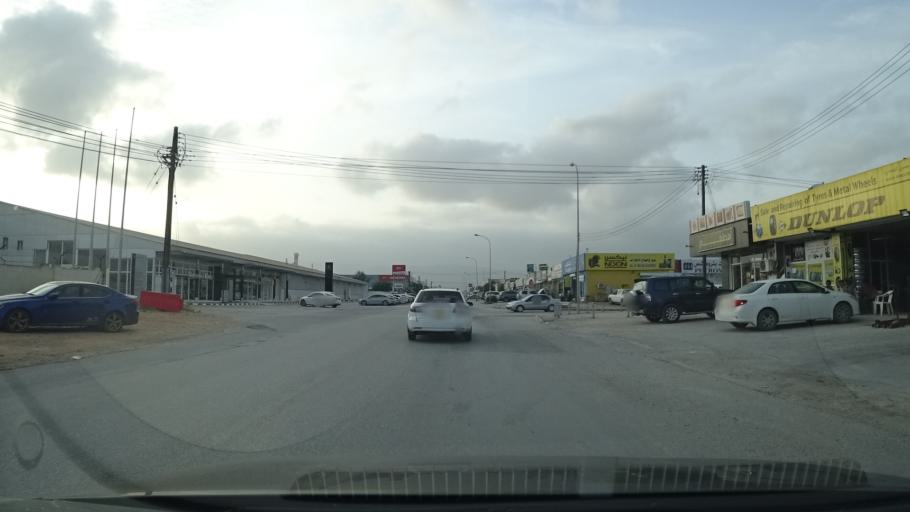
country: OM
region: Zufar
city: Salalah
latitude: 17.0136
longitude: 54.0466
